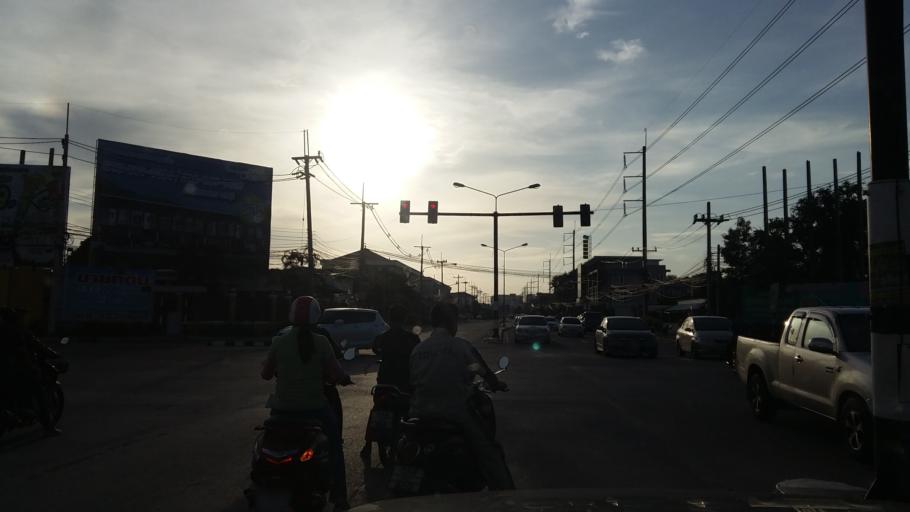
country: TH
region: Chon Buri
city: Chon Buri
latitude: 13.2776
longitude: 100.9446
